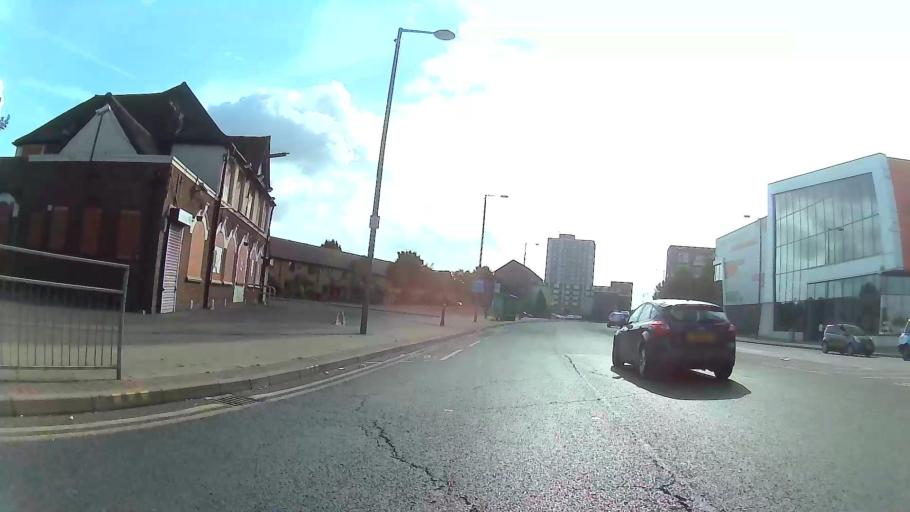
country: GB
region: England
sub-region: Greater London
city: Chadwell Heath
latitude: 51.5613
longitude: 0.1484
